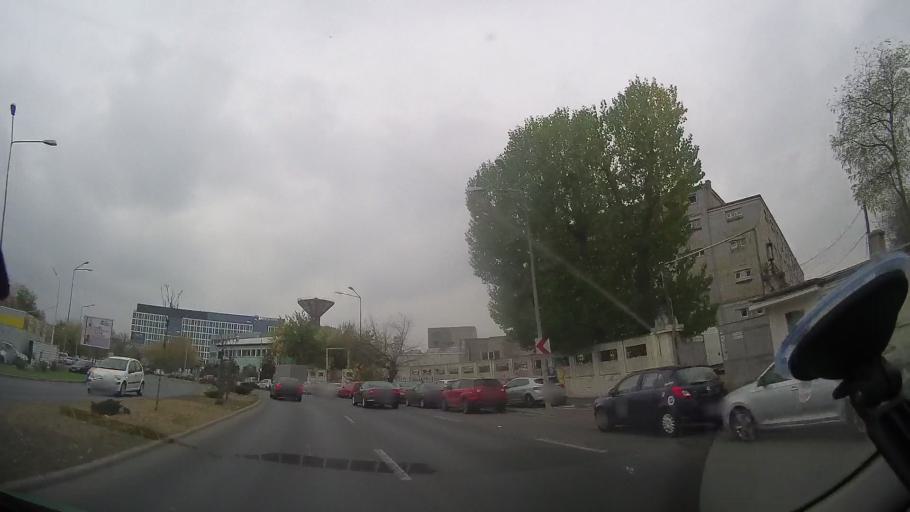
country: RO
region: Bucuresti
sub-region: Municipiul Bucuresti
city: Bucuresti
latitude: 44.4213
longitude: 26.0742
